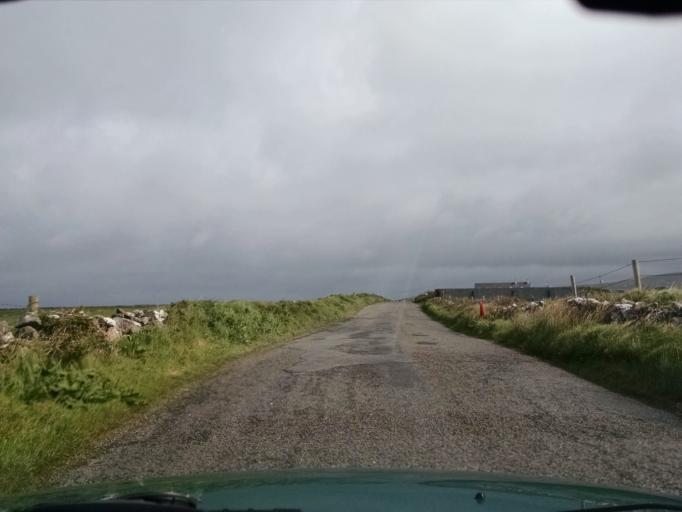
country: IE
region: Connaught
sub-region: County Galway
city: Bearna
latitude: 53.0299
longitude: -9.3665
